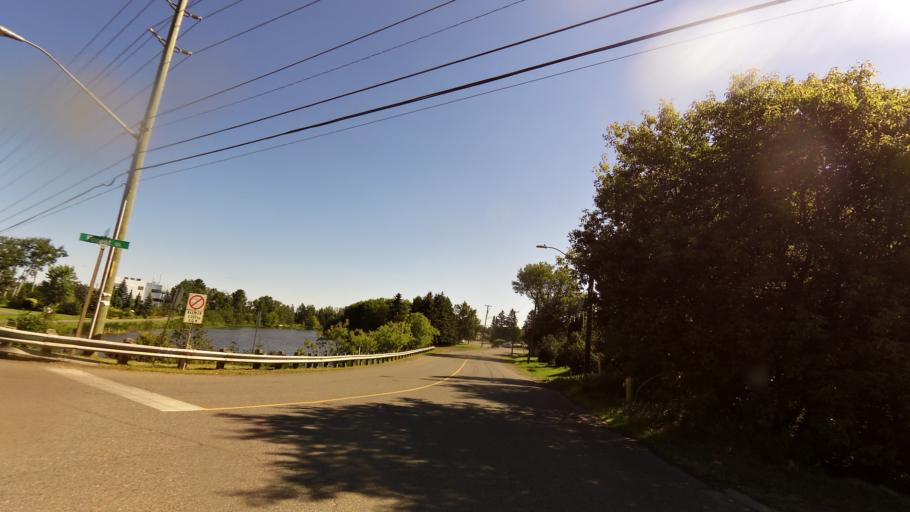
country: CA
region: Ontario
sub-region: Thunder Bay District
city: Thunder Bay
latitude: 48.3975
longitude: -89.2582
